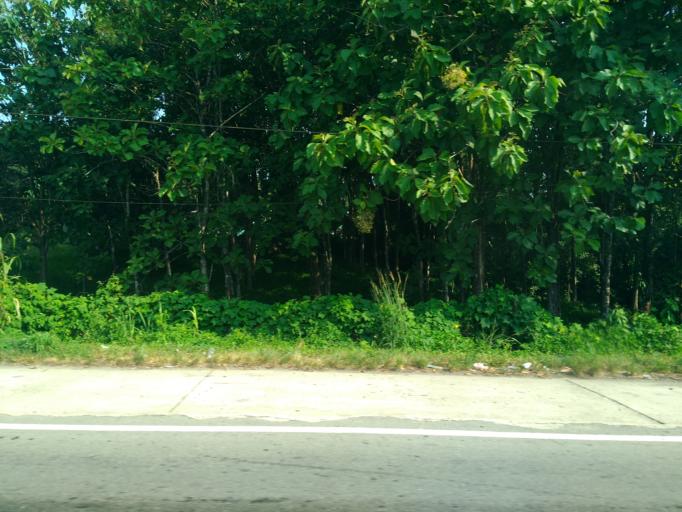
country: MY
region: Sabah
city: Taman Rajawali
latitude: 5.6982
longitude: 117.4041
